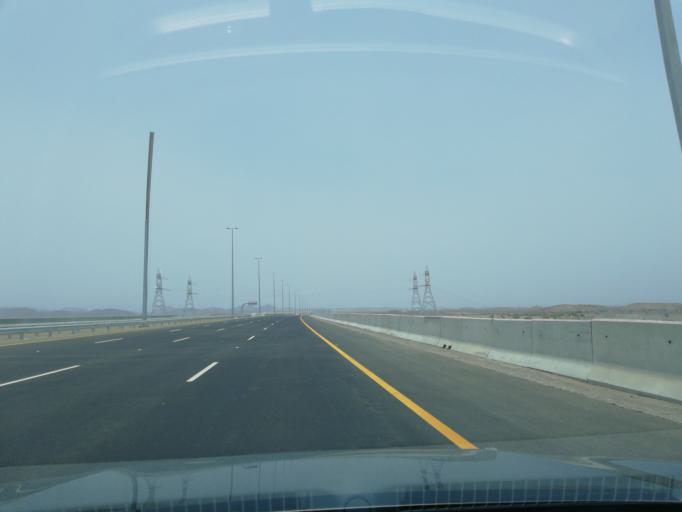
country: OM
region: Al Batinah
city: Al Liwa'
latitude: 24.4256
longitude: 56.5294
